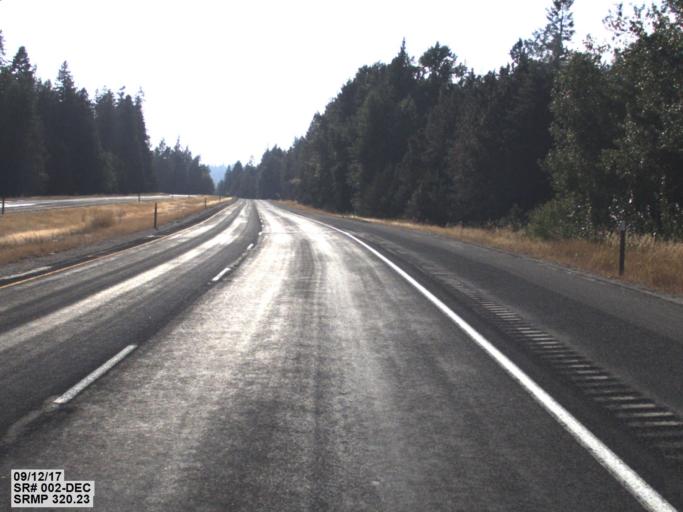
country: US
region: Washington
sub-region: Spokane County
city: Deer Park
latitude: 48.0987
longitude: -117.3009
